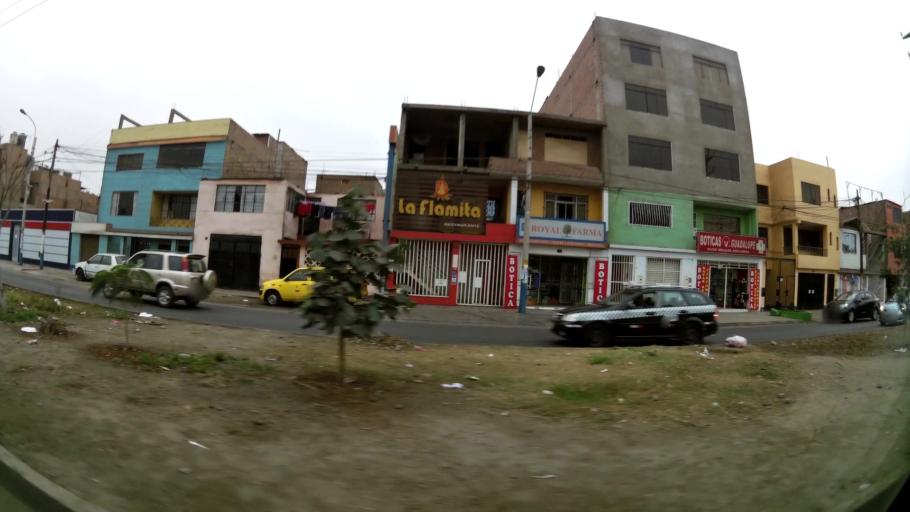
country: PE
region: Lima
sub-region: Lima
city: Independencia
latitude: -11.9388
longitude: -77.0623
